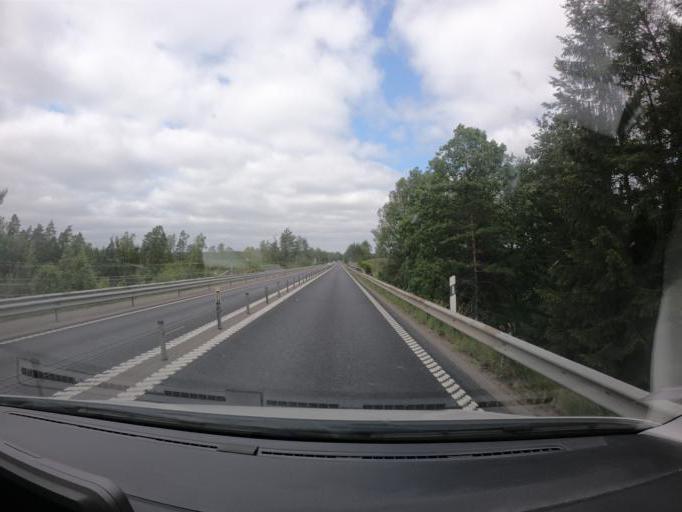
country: SE
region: Skane
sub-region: Perstorps Kommun
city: Perstorp
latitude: 56.1465
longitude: 13.5361
